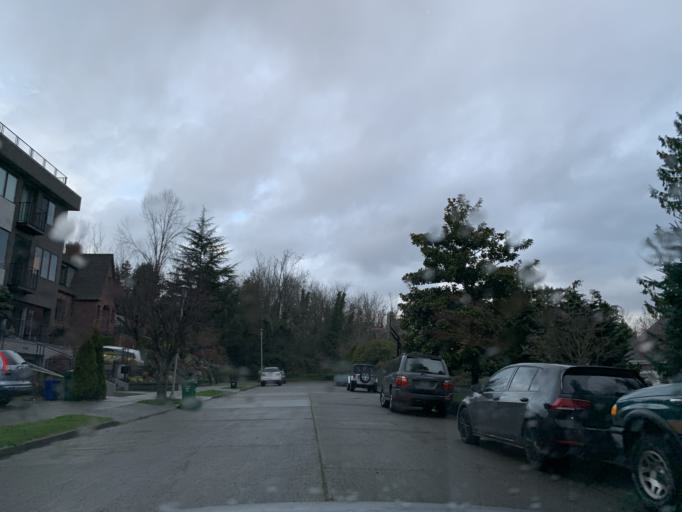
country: US
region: Washington
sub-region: King County
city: Yarrow Point
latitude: 47.6624
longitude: -122.2688
